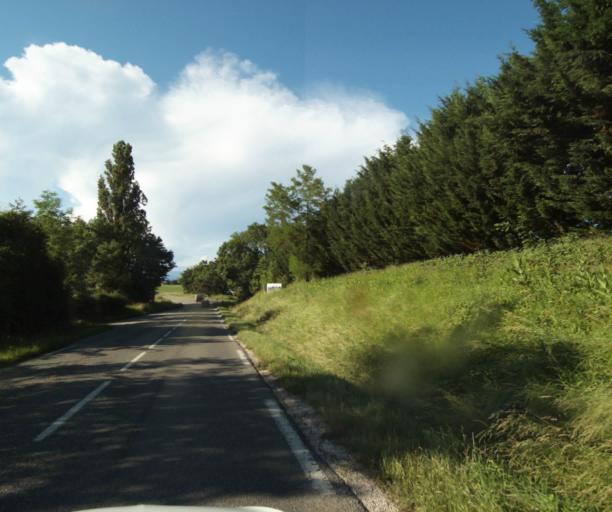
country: FR
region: Rhone-Alpes
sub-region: Departement de la Haute-Savoie
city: Messery
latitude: 46.3431
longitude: 6.2921
